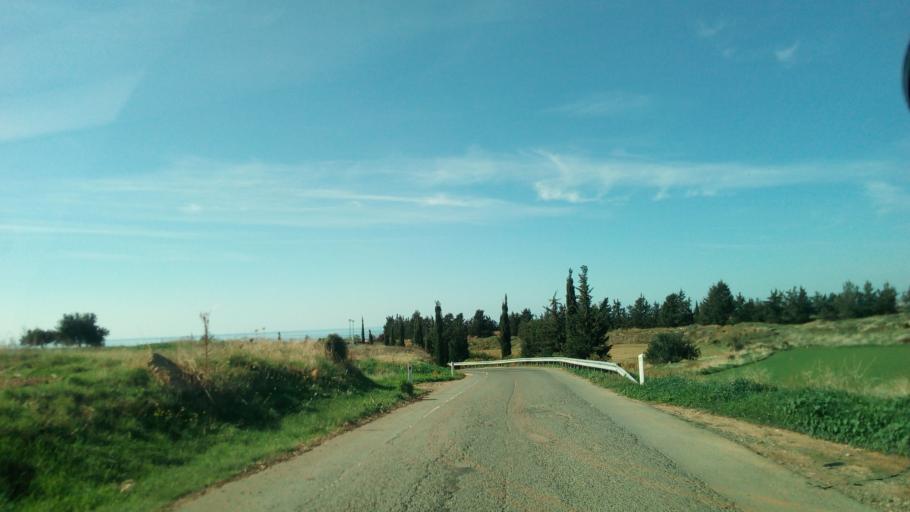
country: CY
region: Limassol
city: Pissouri
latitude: 34.7128
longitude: 32.5814
